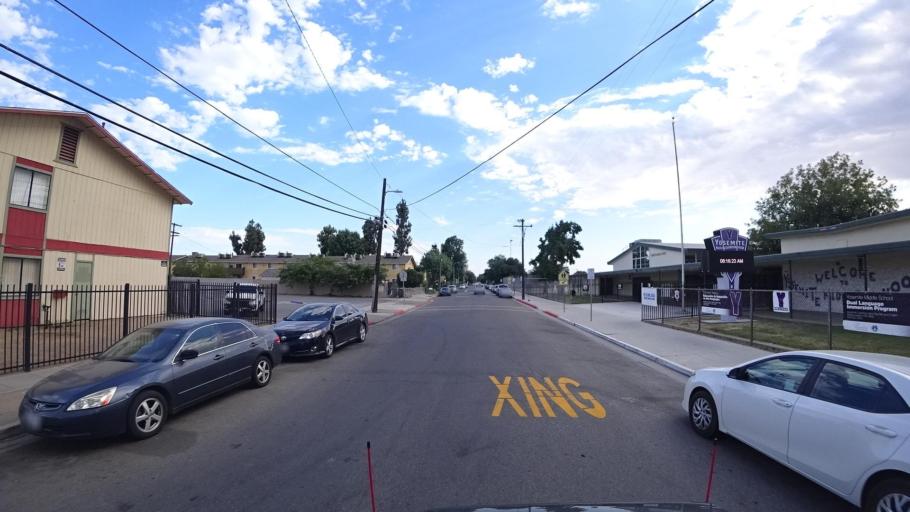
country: US
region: California
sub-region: Fresno County
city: Fresno
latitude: 36.7591
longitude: -119.7590
